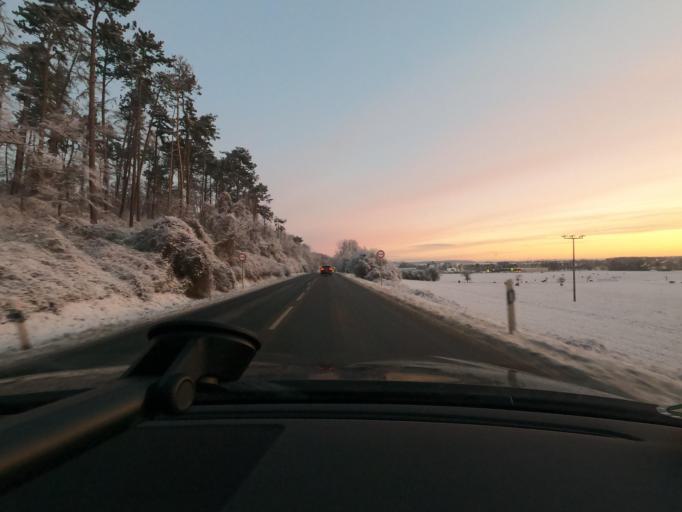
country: DE
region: Thuringia
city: Kallmerode
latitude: 51.3707
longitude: 10.3096
